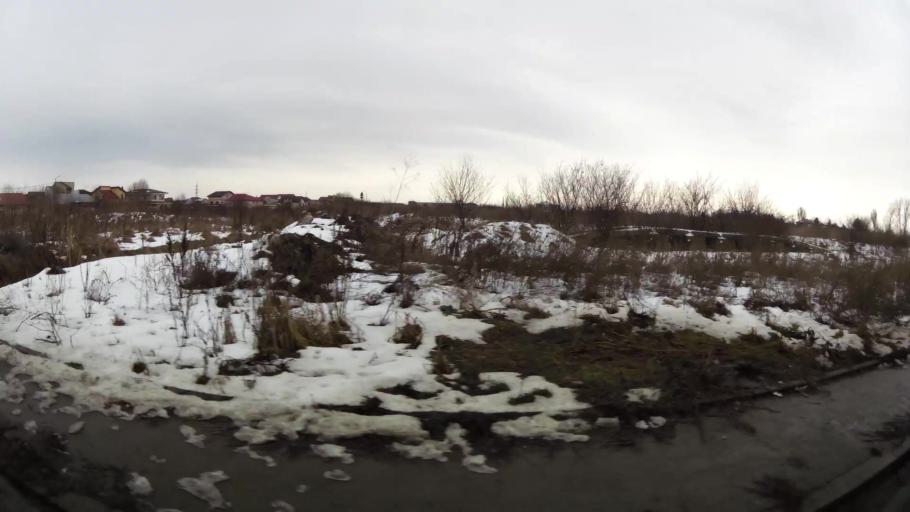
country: RO
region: Ilfov
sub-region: Comuna Pantelimon
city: Pantelimon
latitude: 44.4560
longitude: 26.2141
